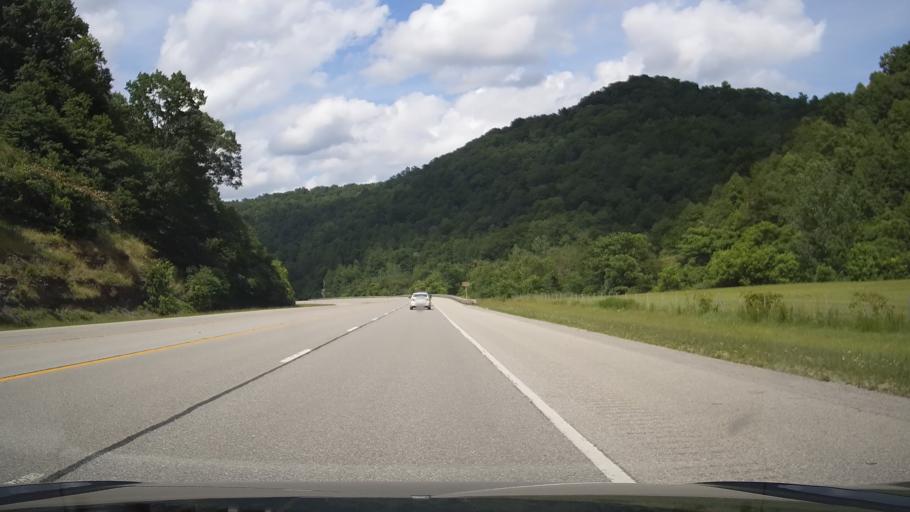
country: US
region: Kentucky
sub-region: Letcher County
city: Jenkins
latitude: 37.2510
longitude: -82.6179
